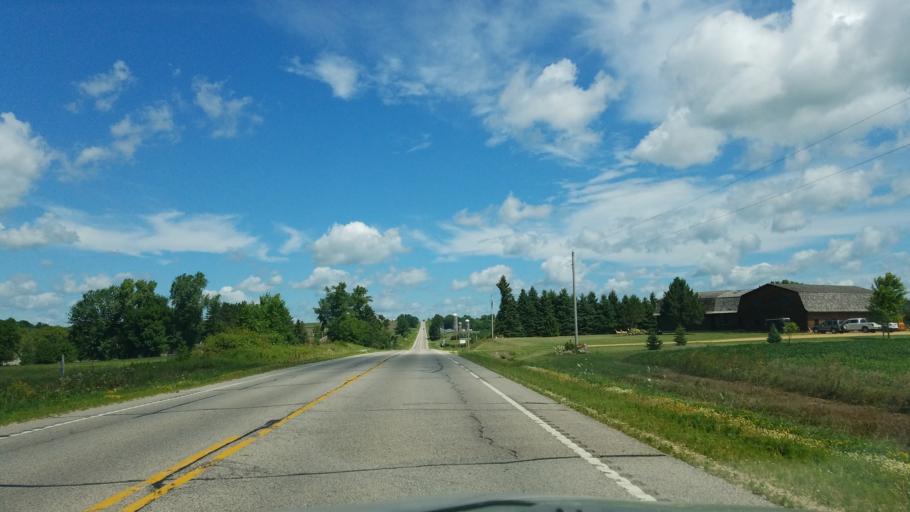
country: US
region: Wisconsin
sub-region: Saint Croix County
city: Glenwood City
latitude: 44.9998
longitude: -92.1966
